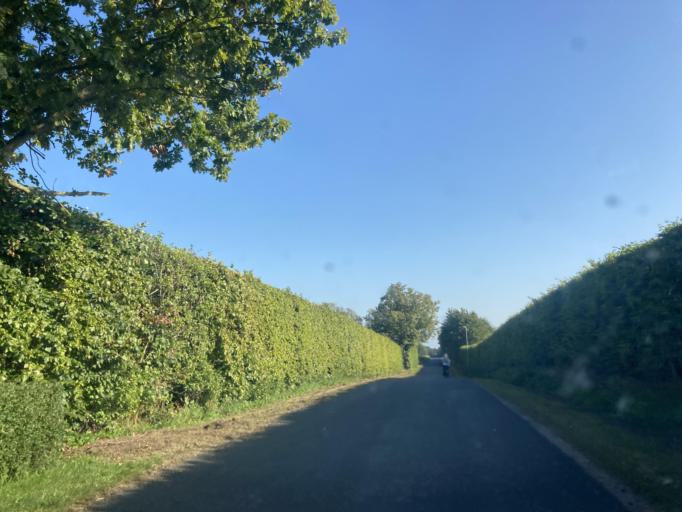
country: DK
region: South Denmark
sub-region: Svendborg Kommune
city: Thuro By
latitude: 55.1191
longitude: 10.7302
